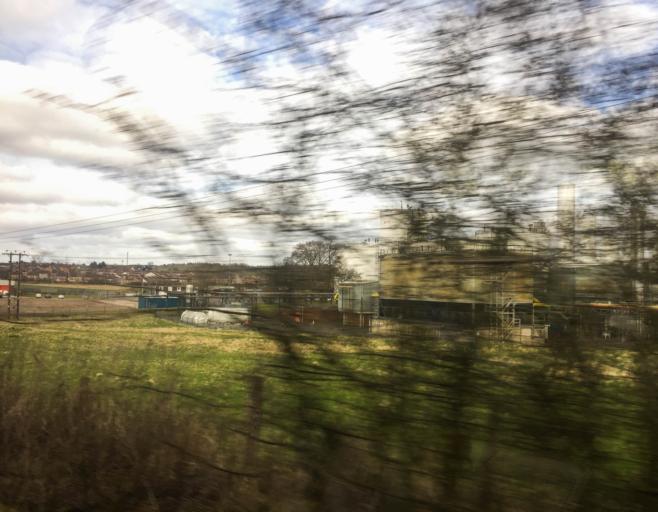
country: GB
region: Scotland
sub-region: North Lanarkshire
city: Newarthill
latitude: 55.8002
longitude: -3.9538
